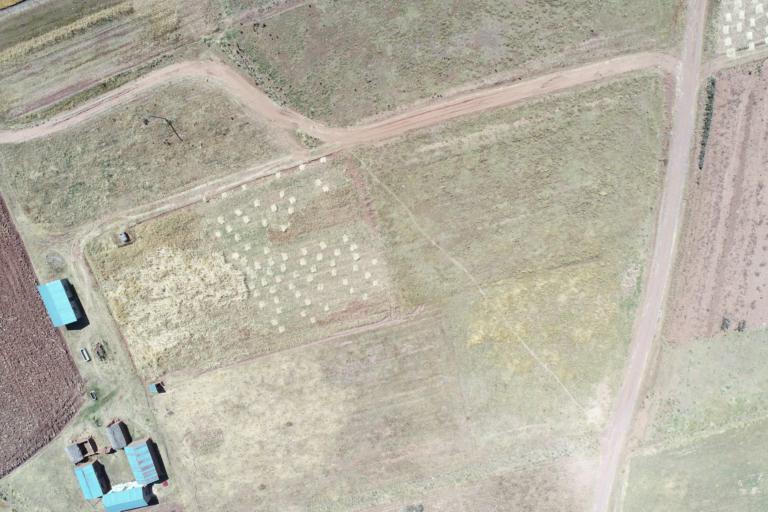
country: BO
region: La Paz
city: Tiahuanaco
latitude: -16.5924
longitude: -68.7722
